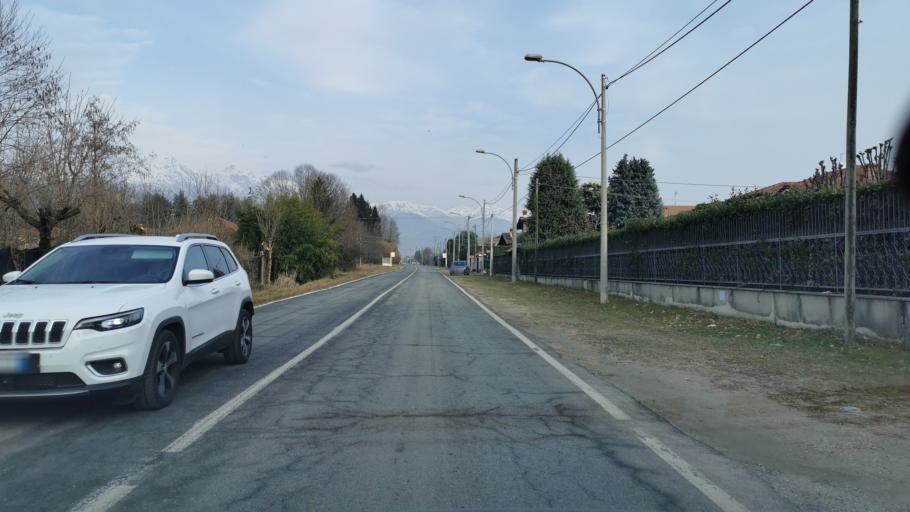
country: IT
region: Piedmont
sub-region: Provincia di Torino
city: Oglianico
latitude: 45.3474
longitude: 7.6922
